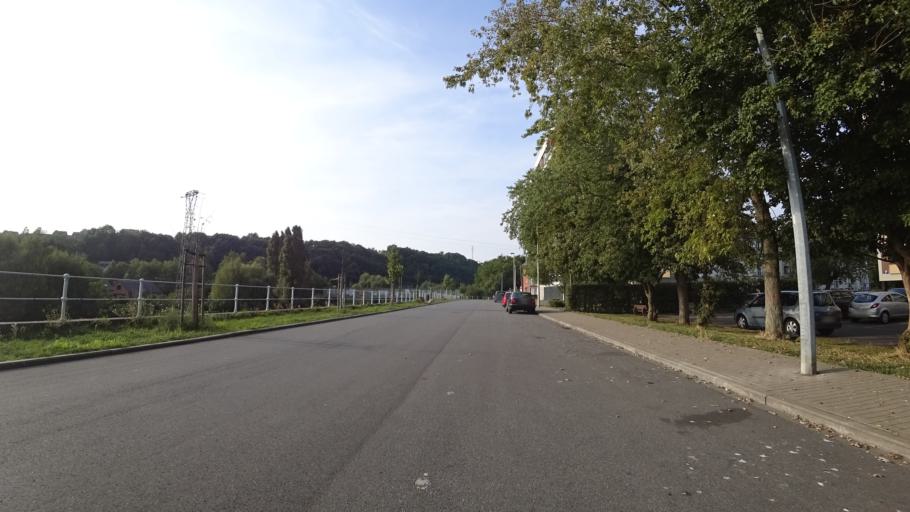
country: BE
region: Wallonia
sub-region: Province de Namur
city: Namur
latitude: 50.4590
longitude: 4.8336
